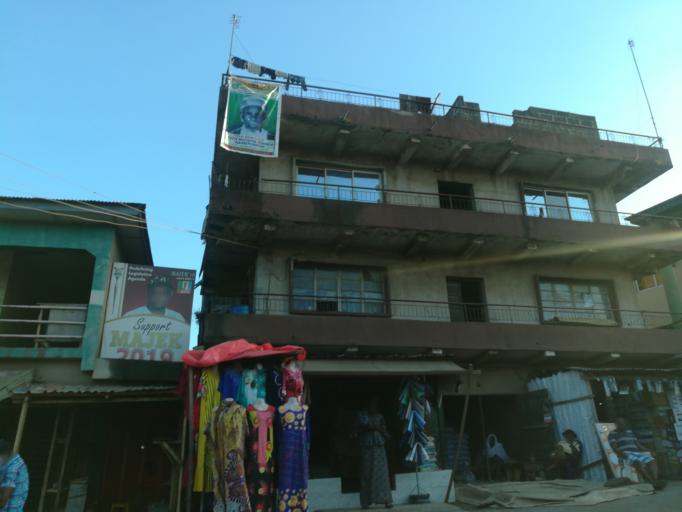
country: NG
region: Lagos
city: Ikorodu
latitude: 6.6185
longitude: 3.5073
